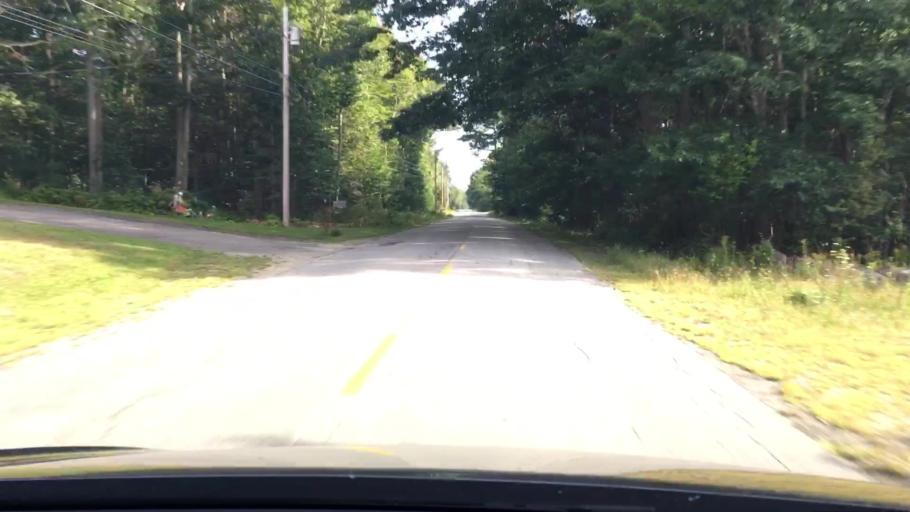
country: US
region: Maine
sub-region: Hancock County
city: Bucksport
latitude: 44.5399
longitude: -68.7952
